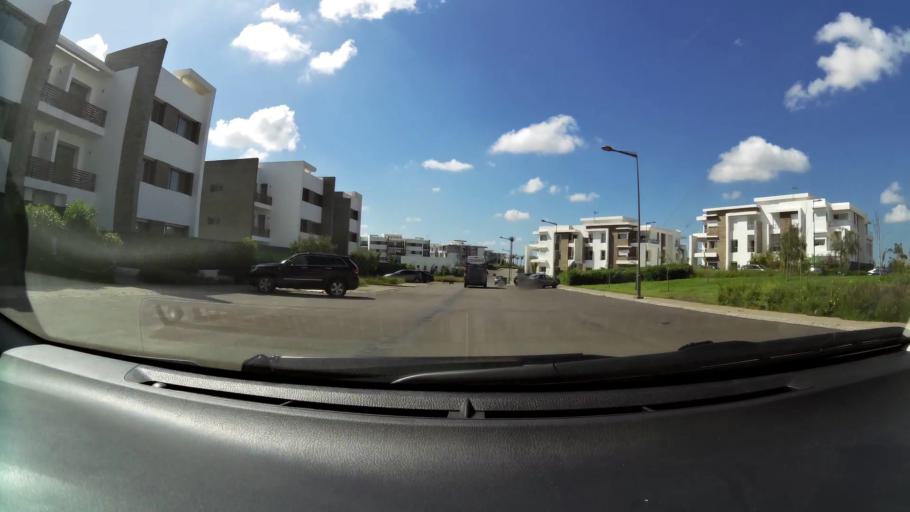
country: MA
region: Grand Casablanca
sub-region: Nouaceur
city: Bouskoura
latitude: 33.4735
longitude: -7.6029
